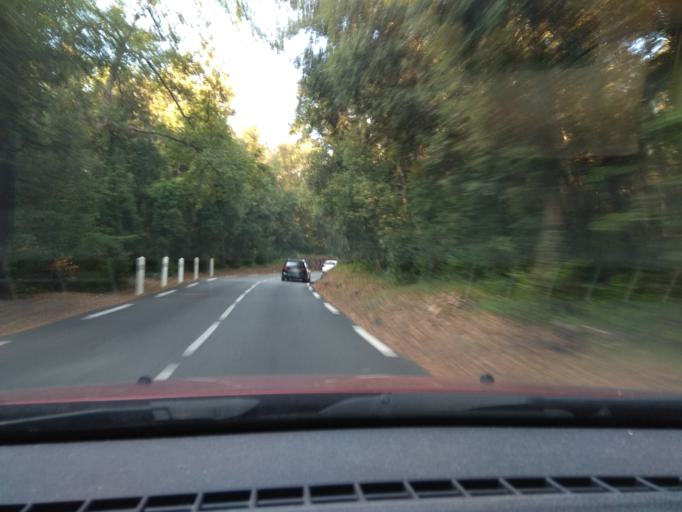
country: FR
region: Provence-Alpes-Cote d'Azur
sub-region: Departement des Alpes-Maritimes
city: Le Rouret
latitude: 43.6600
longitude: 7.0304
